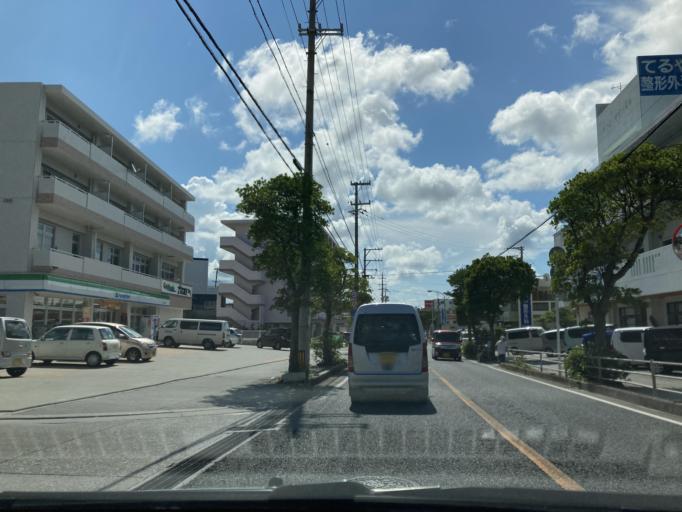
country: JP
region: Okinawa
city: Tomigusuku
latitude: 26.1842
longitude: 127.7126
